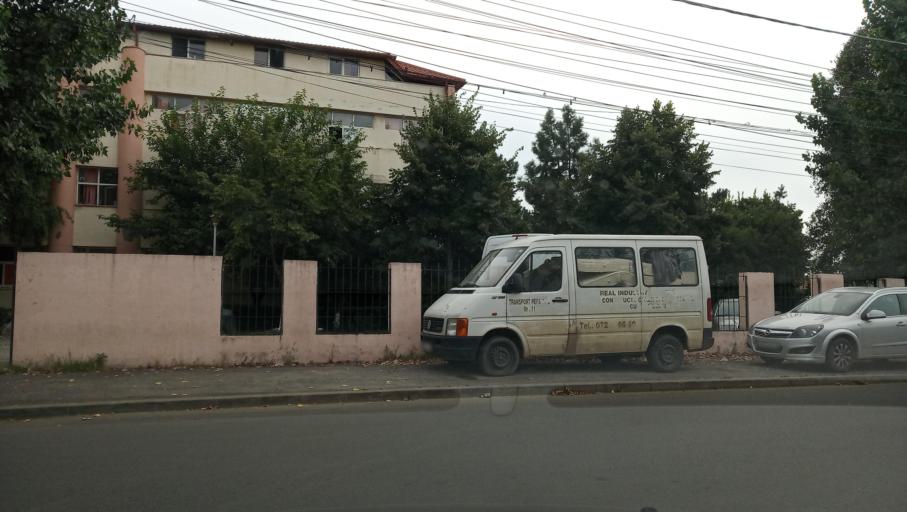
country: RO
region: Ilfov
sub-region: Comuna Pantelimon
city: Pantelimon
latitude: 44.4266
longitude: 26.2010
